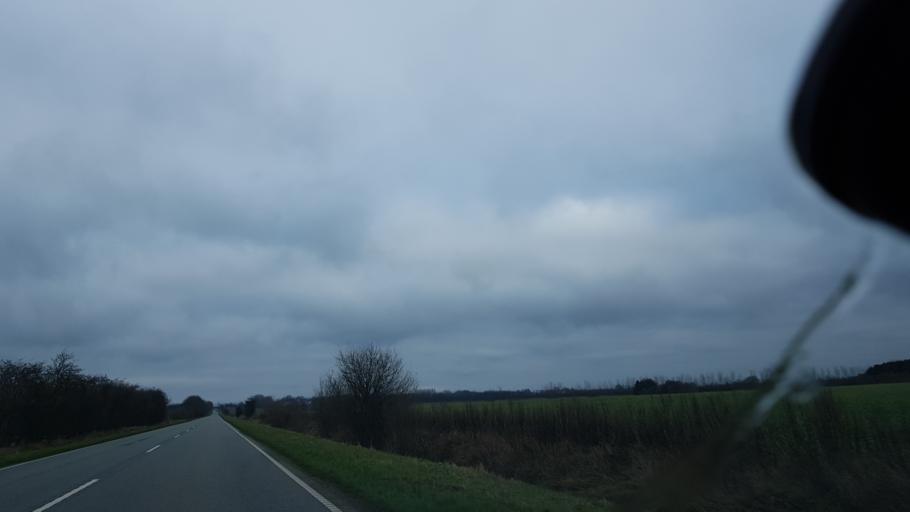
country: DK
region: South Denmark
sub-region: Haderslev Kommune
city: Vojens
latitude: 55.2316
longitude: 9.2101
